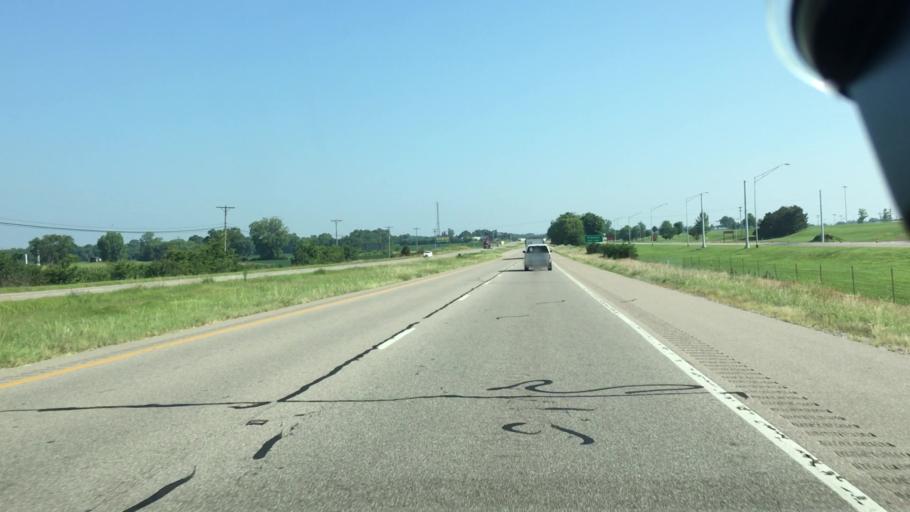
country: US
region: Indiana
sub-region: Gibson County
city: Fort Branch
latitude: 38.2938
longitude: -87.5674
